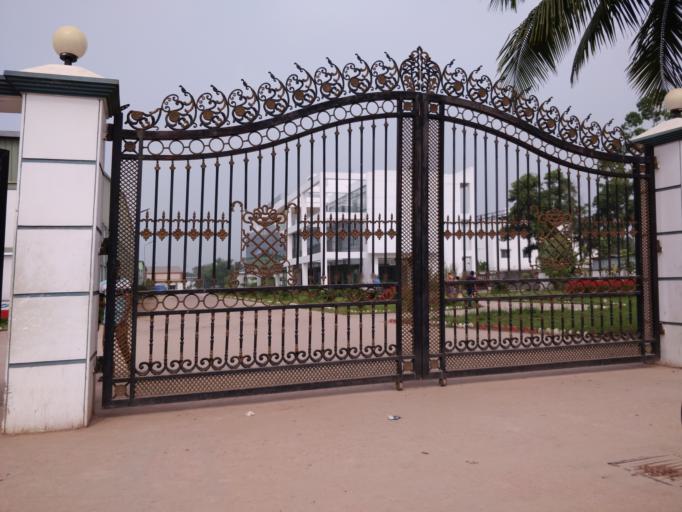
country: BD
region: Sylhet
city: Habiganj
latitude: 24.1720
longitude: 91.3554
